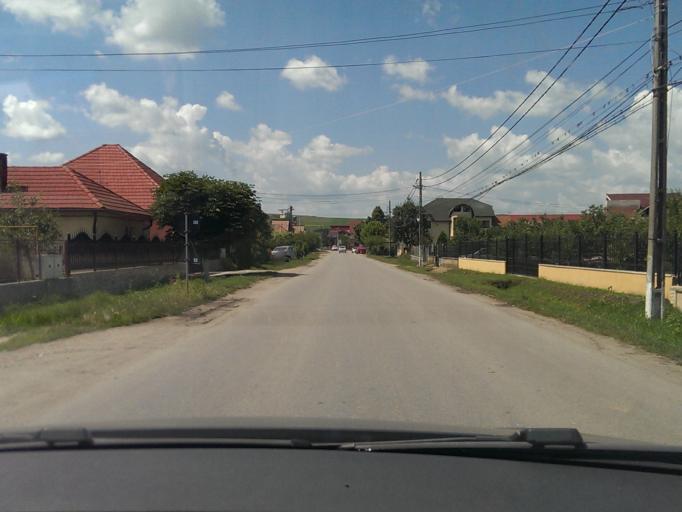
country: RO
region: Cluj
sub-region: Comuna Apahida
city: Sannicoara
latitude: 46.7906
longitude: 23.7249
